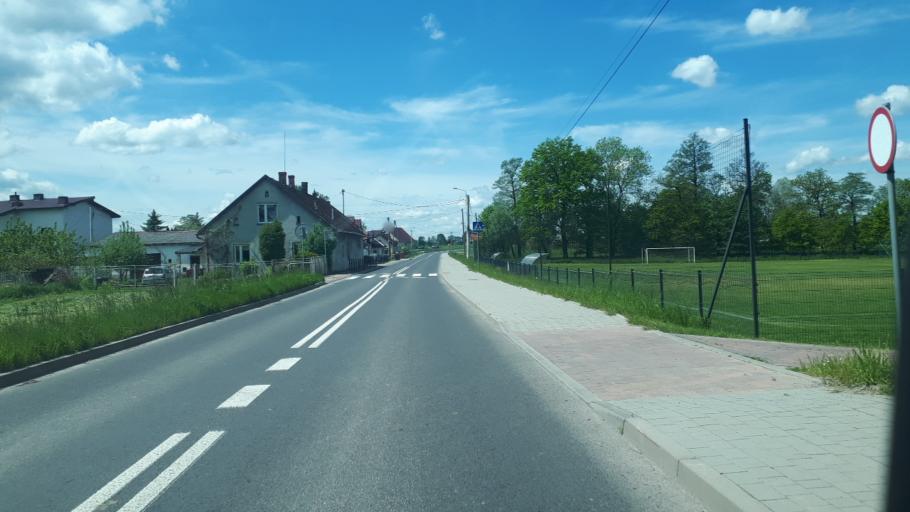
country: PL
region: Silesian Voivodeship
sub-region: Powiat bielski
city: Bronow
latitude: 49.8764
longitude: 18.9182
